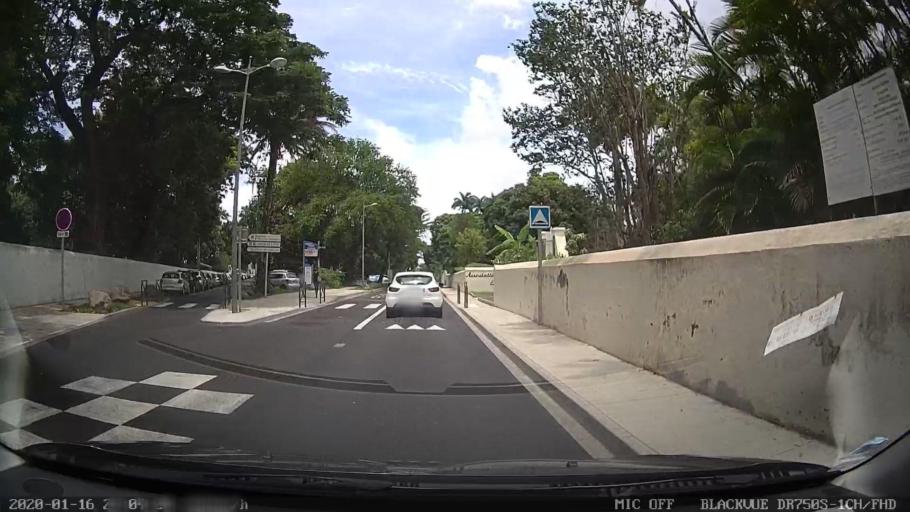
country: RE
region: Reunion
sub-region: Reunion
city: Saint-Denis
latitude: -20.8880
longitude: 55.4502
